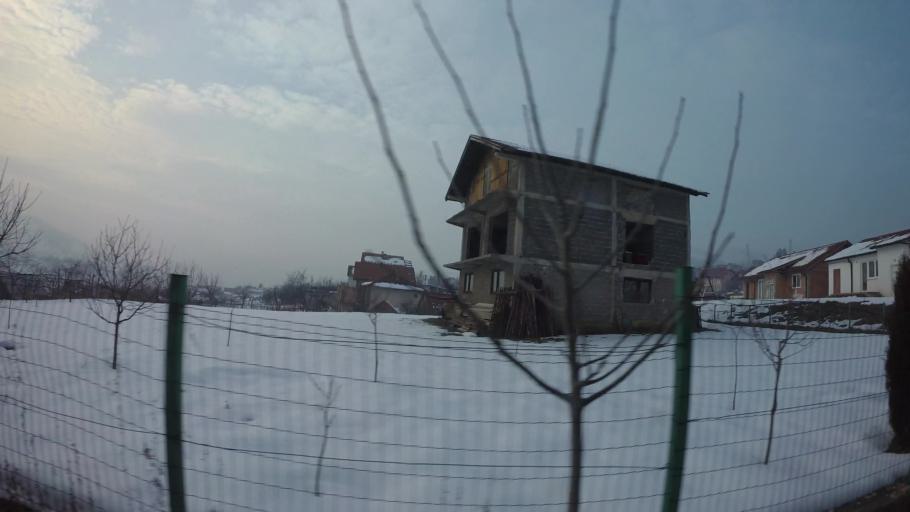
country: BA
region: Federation of Bosnia and Herzegovina
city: Hotonj
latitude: 43.8981
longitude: 18.3793
